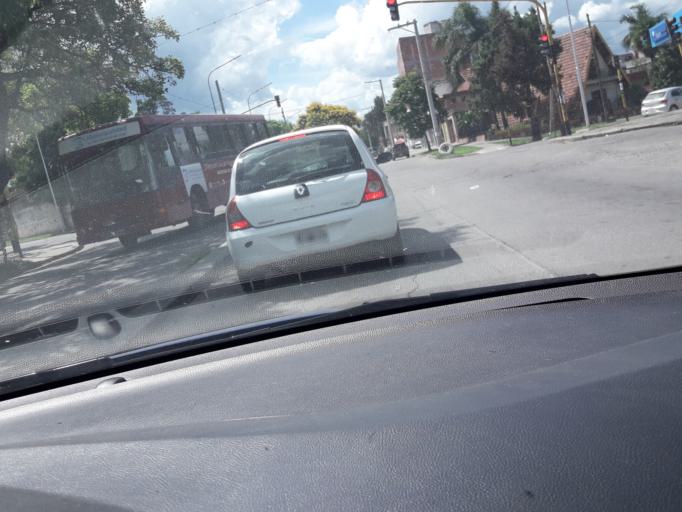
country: AR
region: Jujuy
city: San Salvador de Jujuy
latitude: -24.2047
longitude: -65.2949
